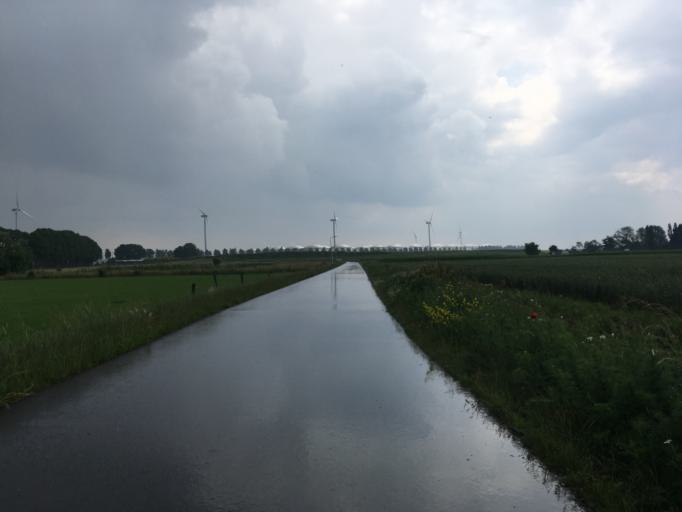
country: NL
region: North Holland
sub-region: Gemeente Velsen
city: Velsen-Zuid
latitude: 52.4193
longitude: 4.7249
